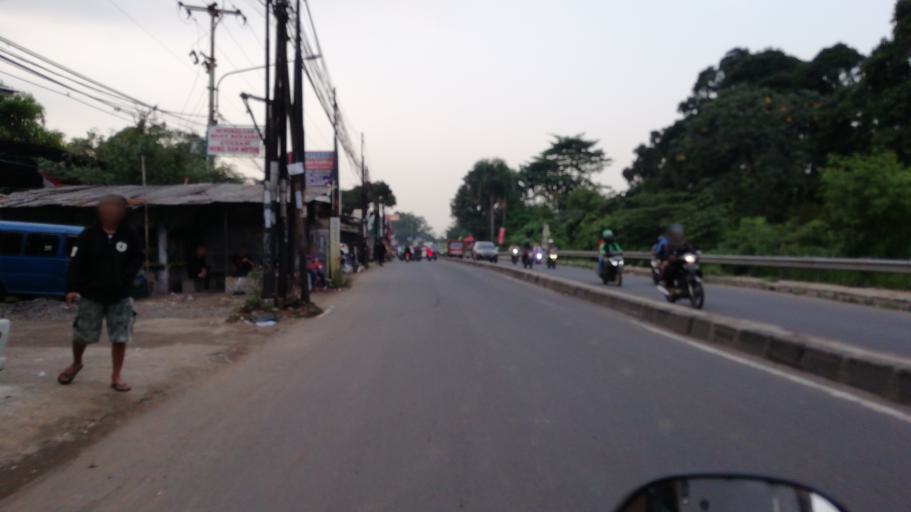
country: ID
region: West Java
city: Cibinong
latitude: -6.4557
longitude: 106.8554
